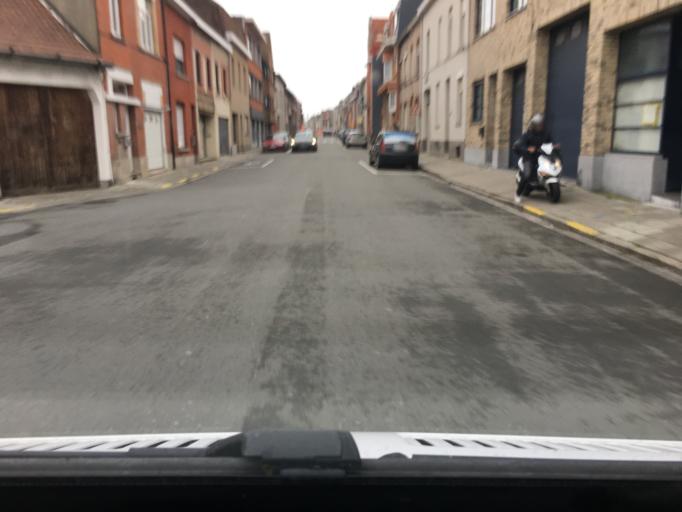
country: BE
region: Flanders
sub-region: Provincie West-Vlaanderen
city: Menen
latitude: 50.7959
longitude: 3.1110
